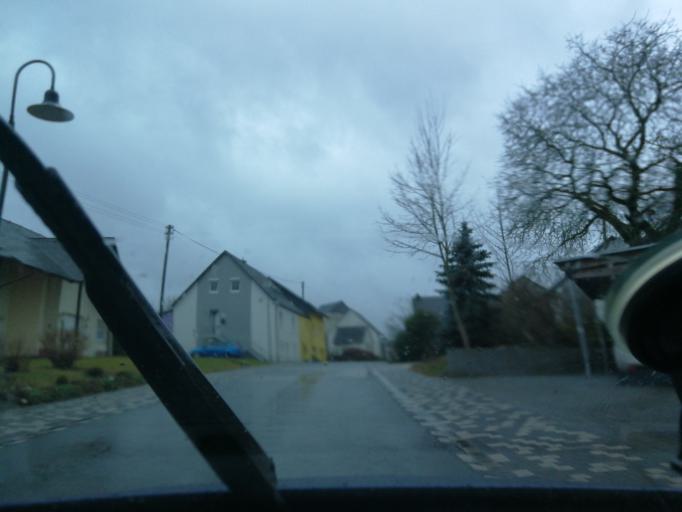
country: DE
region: Rheinland-Pfalz
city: Thalfang
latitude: 49.7466
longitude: 7.0080
